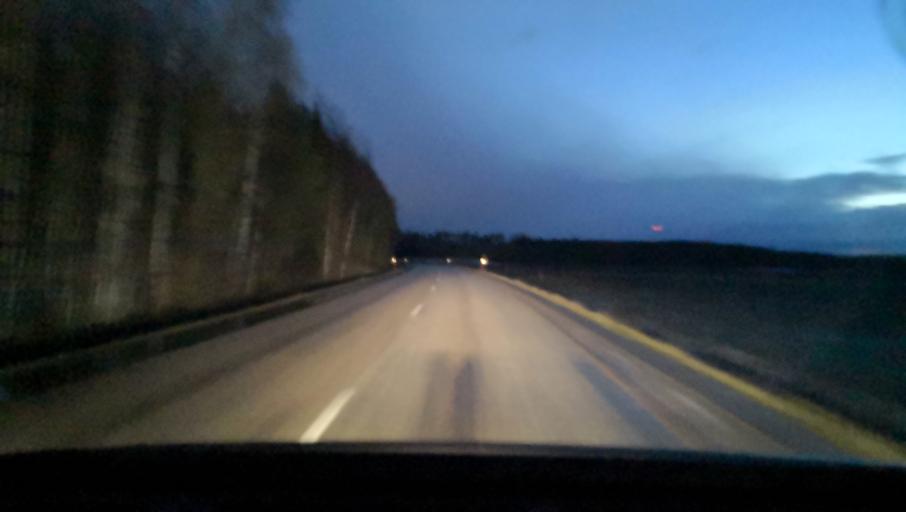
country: SE
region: Vaestmanland
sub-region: Vasteras
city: Skultuna
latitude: 59.7466
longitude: 16.4544
